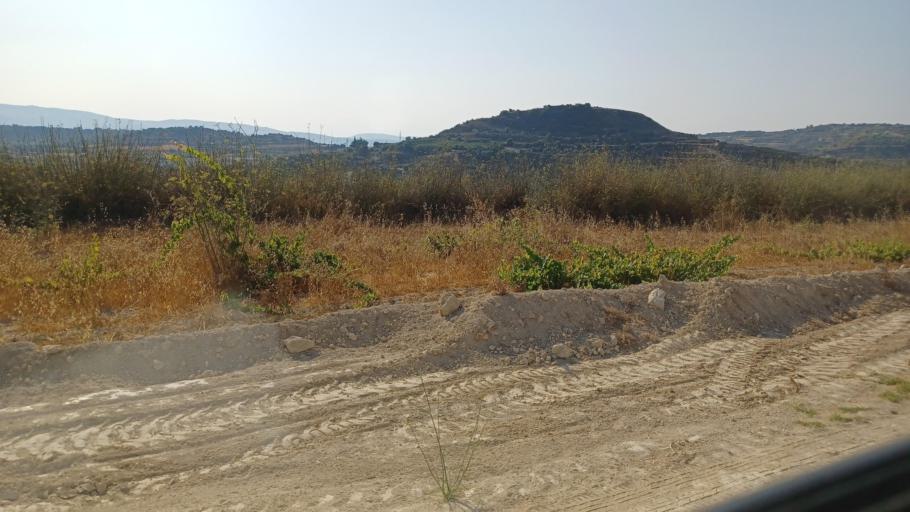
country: CY
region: Pafos
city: Tala
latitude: 34.8800
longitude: 32.4766
